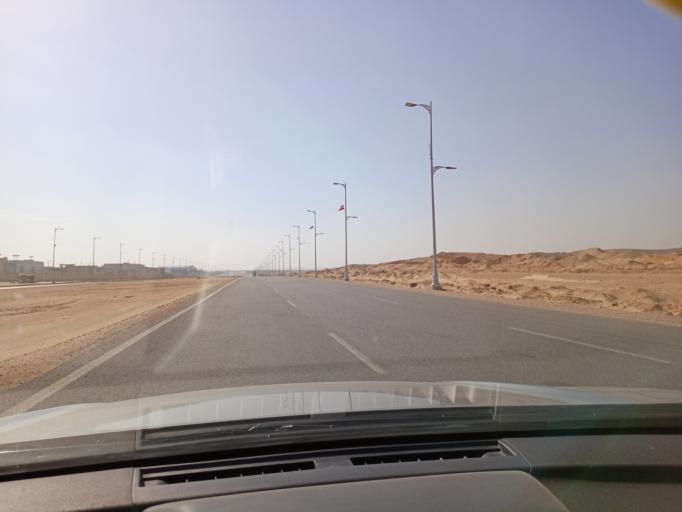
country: EG
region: Muhafazat al Qalyubiyah
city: Al Khankah
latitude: 30.0444
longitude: 31.7060
